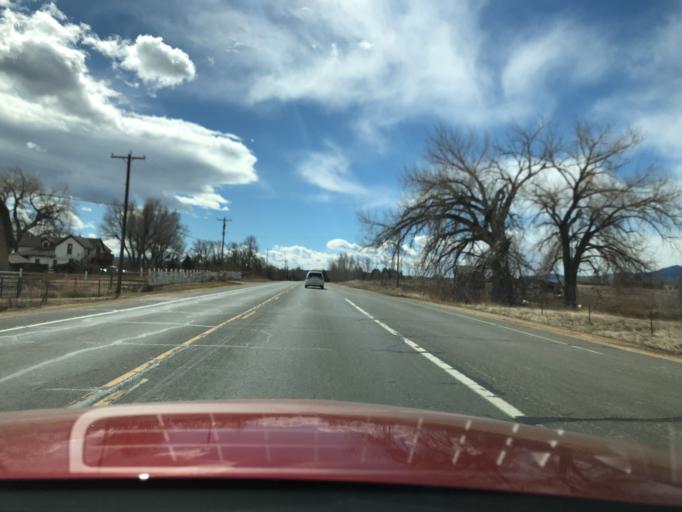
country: US
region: Colorado
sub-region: Boulder County
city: Gunbarrel
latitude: 40.0246
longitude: -105.1788
